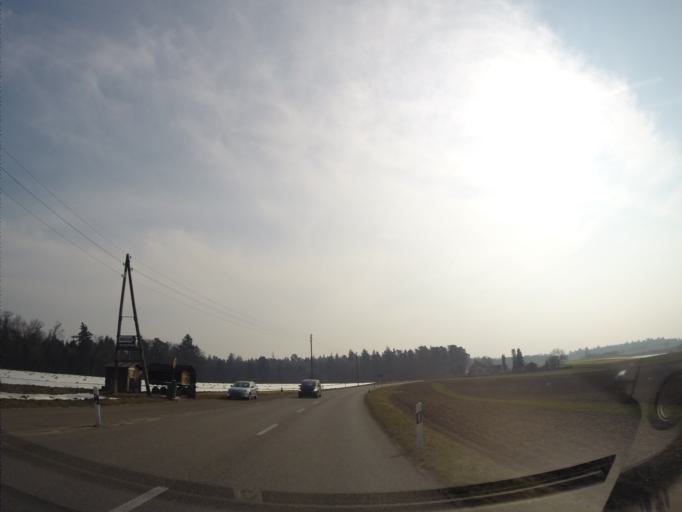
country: CH
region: Zurich
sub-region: Bezirk Andelfingen
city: Kleinandelfingen
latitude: 47.6264
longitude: 8.6931
